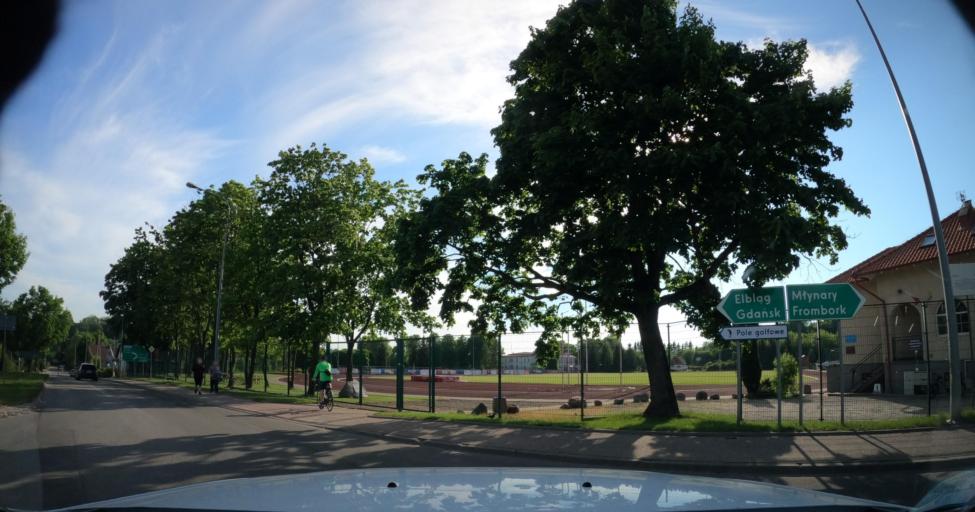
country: PL
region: Warmian-Masurian Voivodeship
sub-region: Powiat elblaski
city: Paslek
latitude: 54.0724
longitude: 19.6611
